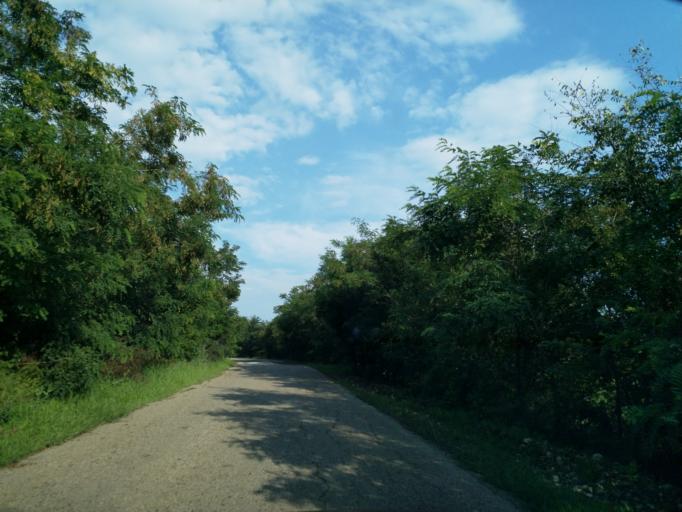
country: RS
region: Central Serbia
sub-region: Pomoravski Okrug
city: Jagodina
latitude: 43.9948
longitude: 21.1962
